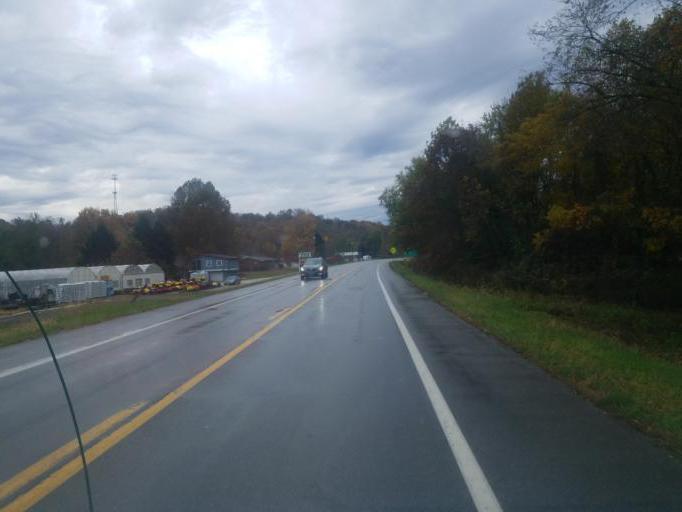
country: US
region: West Virginia
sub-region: Wood County
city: Boaz
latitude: 39.3721
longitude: -81.4812
